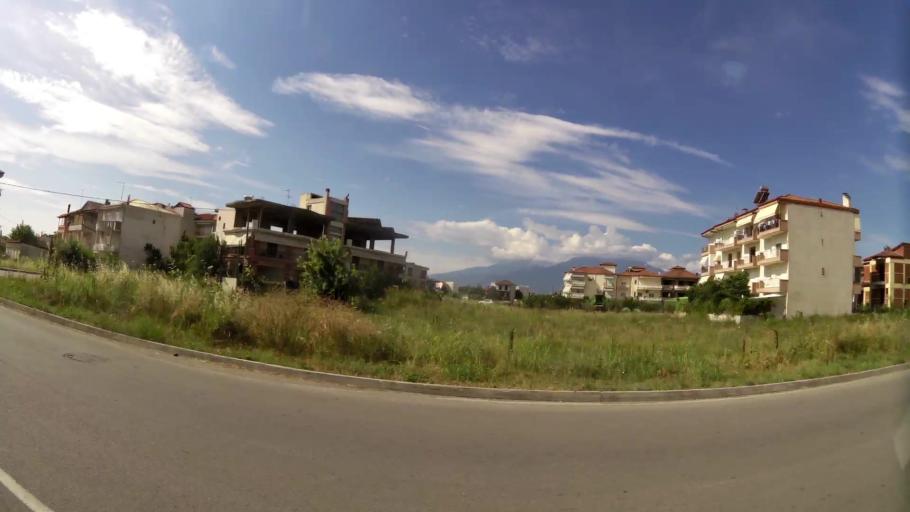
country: GR
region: Central Macedonia
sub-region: Nomos Pierias
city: Katerini
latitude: 40.2805
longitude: 22.4947
